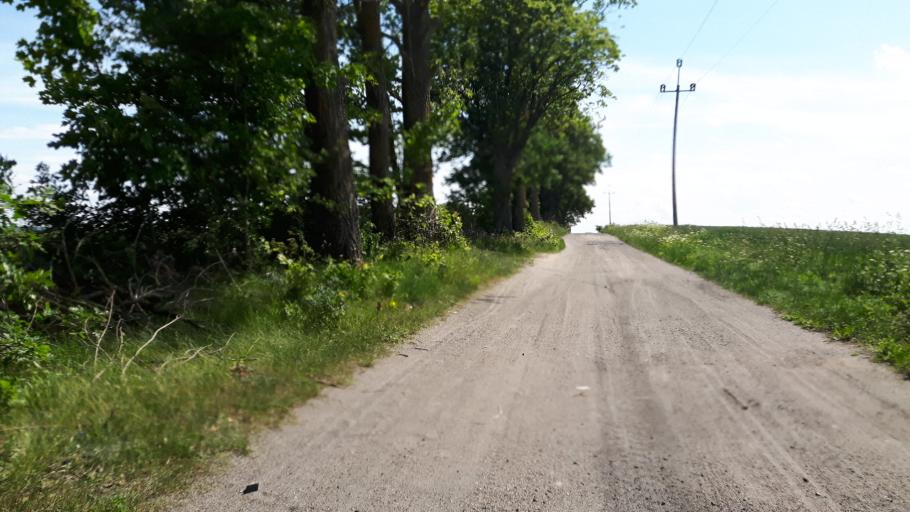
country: PL
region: Pomeranian Voivodeship
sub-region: Powiat wejherowski
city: Gniewino
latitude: 54.7299
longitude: 17.9550
